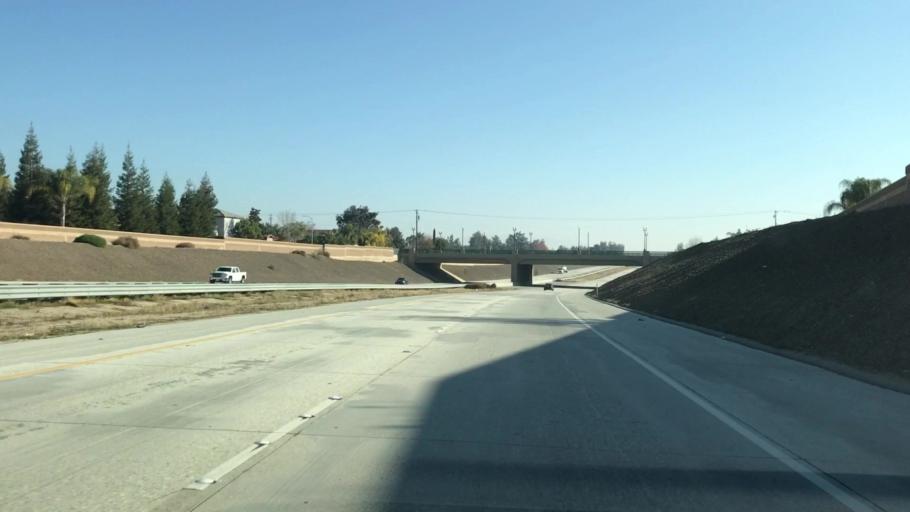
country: US
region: California
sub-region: Kern County
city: Rosedale
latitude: 35.3592
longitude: -119.1660
